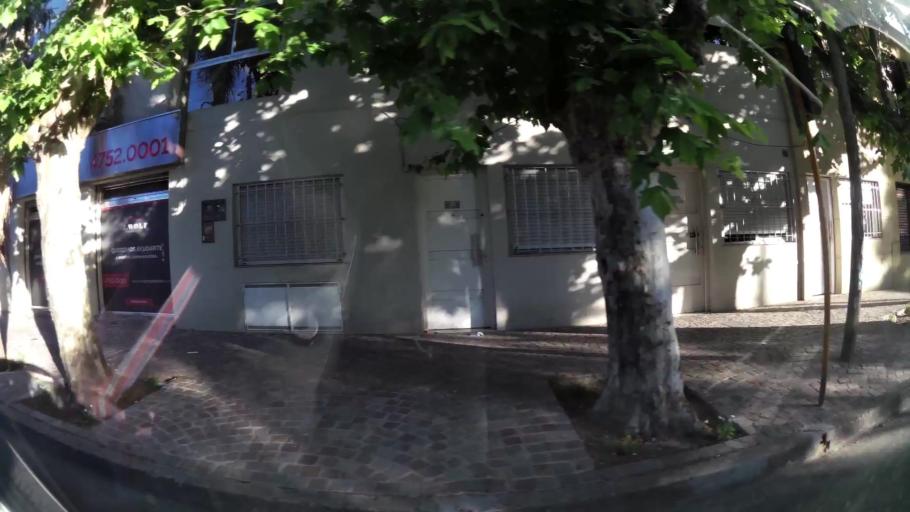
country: AR
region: Buenos Aires
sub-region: Partido de General San Martin
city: General San Martin
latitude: -34.5670
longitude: -58.5434
